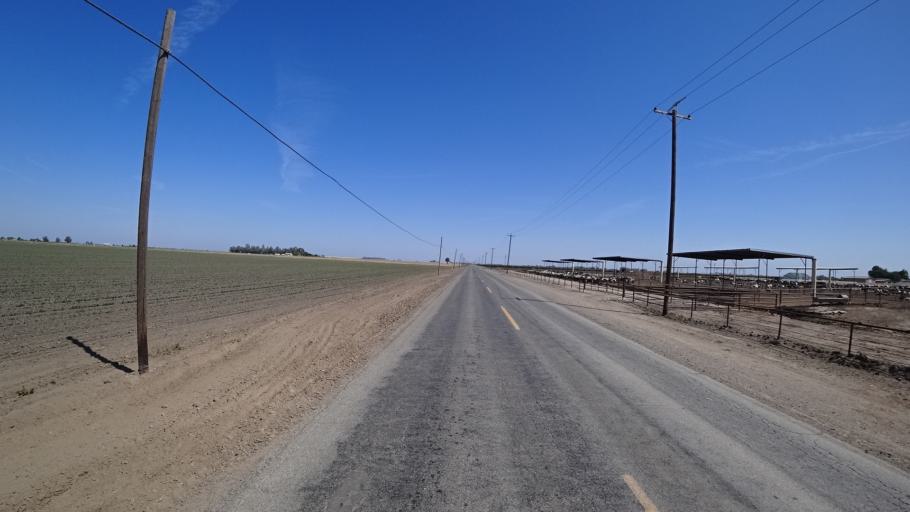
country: US
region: California
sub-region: Kings County
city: Stratford
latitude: 36.2017
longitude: -119.7983
